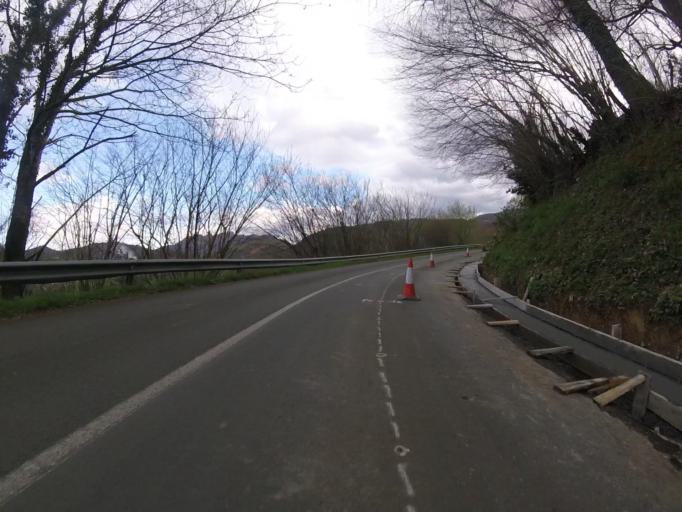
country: ES
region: Basque Country
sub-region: Provincia de Guipuzcoa
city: Errenteria
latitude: 43.2824
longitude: -1.8550
